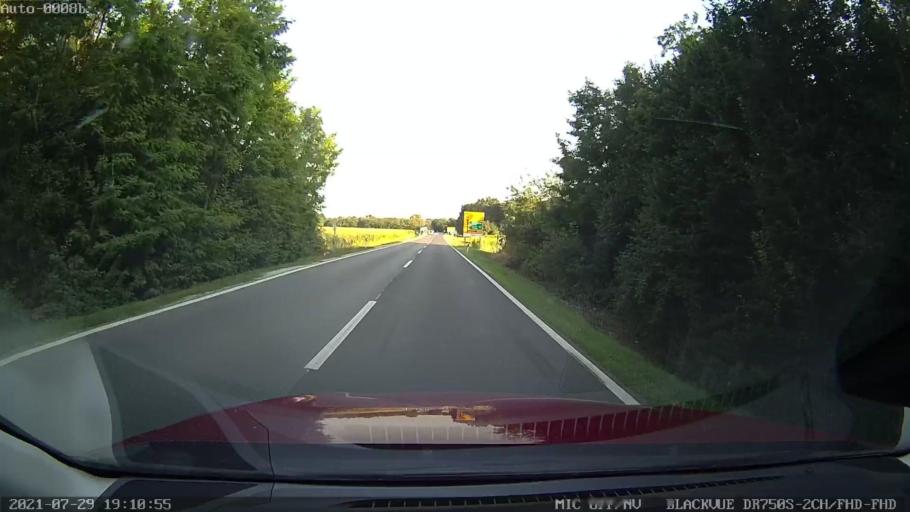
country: HR
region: Varazdinska
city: Jalzabet
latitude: 46.2841
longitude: 16.5055
